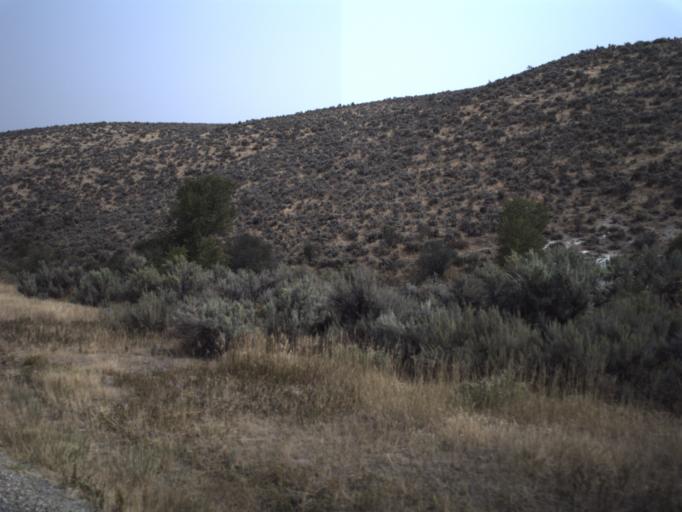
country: US
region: Utah
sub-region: Summit County
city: Coalville
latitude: 40.9763
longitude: -111.5373
